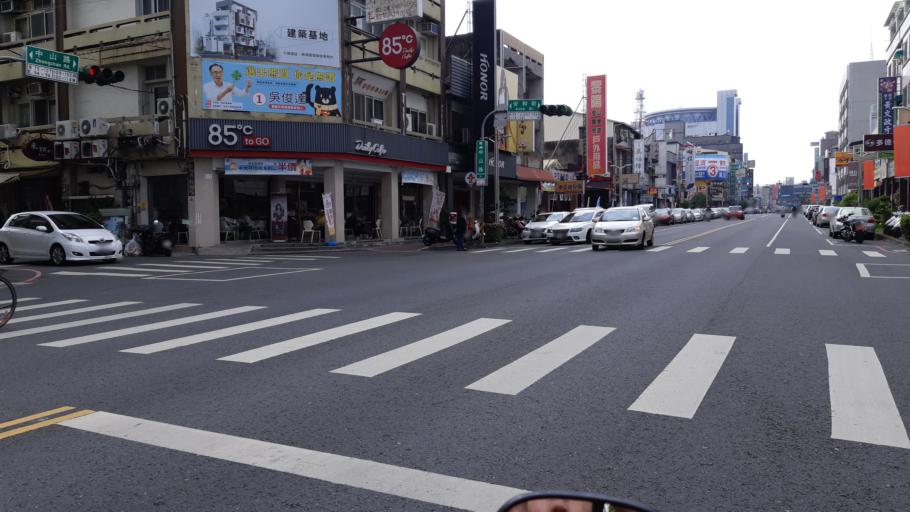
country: TW
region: Taiwan
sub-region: Chiayi
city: Jiayi Shi
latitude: 23.4821
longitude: 120.4579
